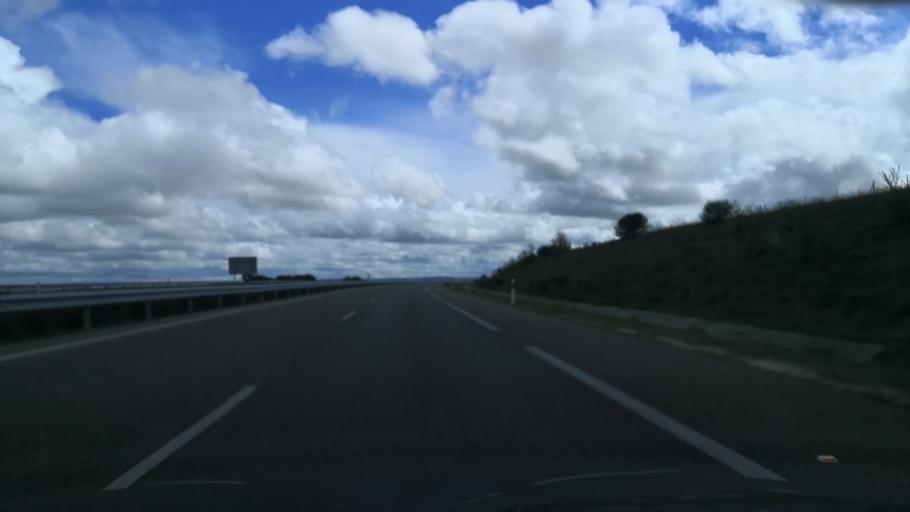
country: ES
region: Castille and Leon
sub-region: Provincia de Zamora
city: Cazurra
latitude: 41.4072
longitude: -5.7186
